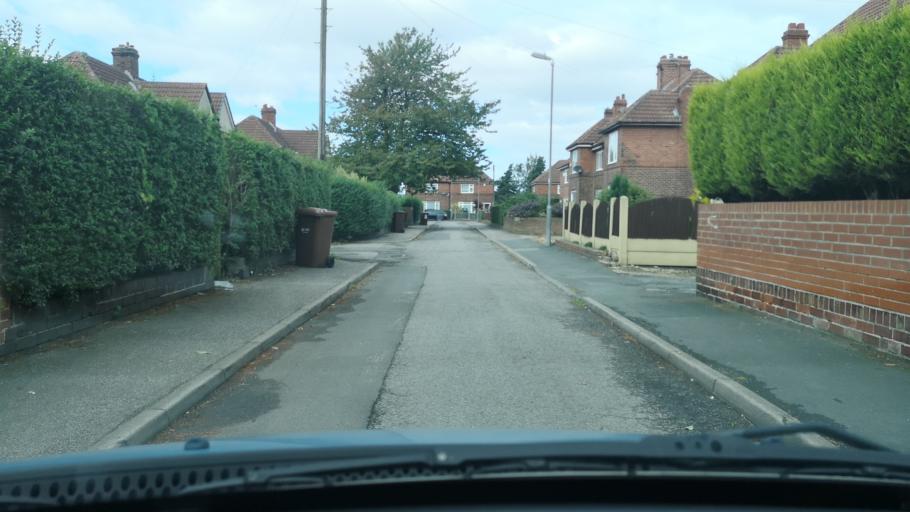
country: GB
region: England
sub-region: City and Borough of Wakefield
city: Fitzwilliam
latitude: 53.6377
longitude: -1.3753
